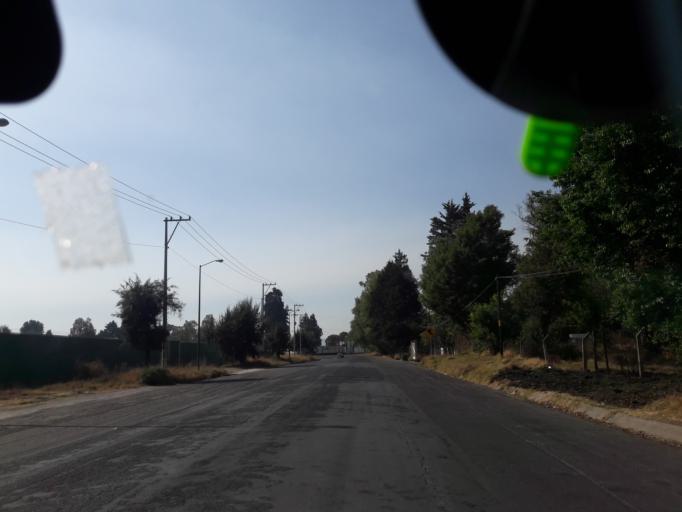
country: MX
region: Tlaxcala
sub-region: Ixtacuixtla de Mariano Matamoros
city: Villa Mariano Matamoros
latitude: 19.3120
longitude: -98.3861
